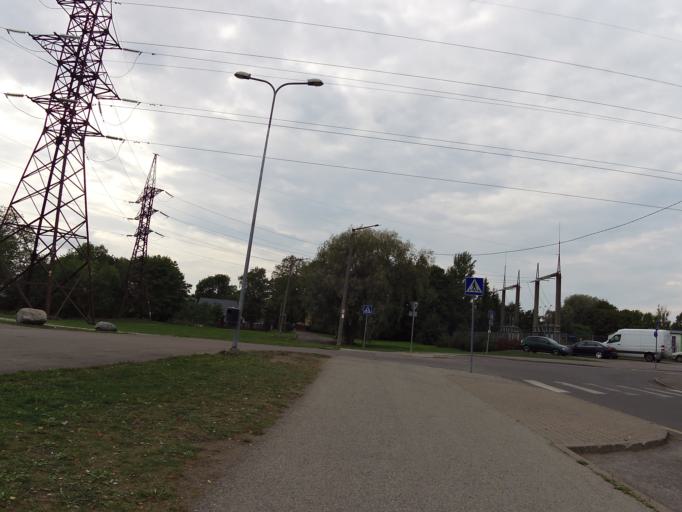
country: EE
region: Harju
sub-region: Tallinna linn
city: Tallinn
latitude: 59.4502
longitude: 24.6844
